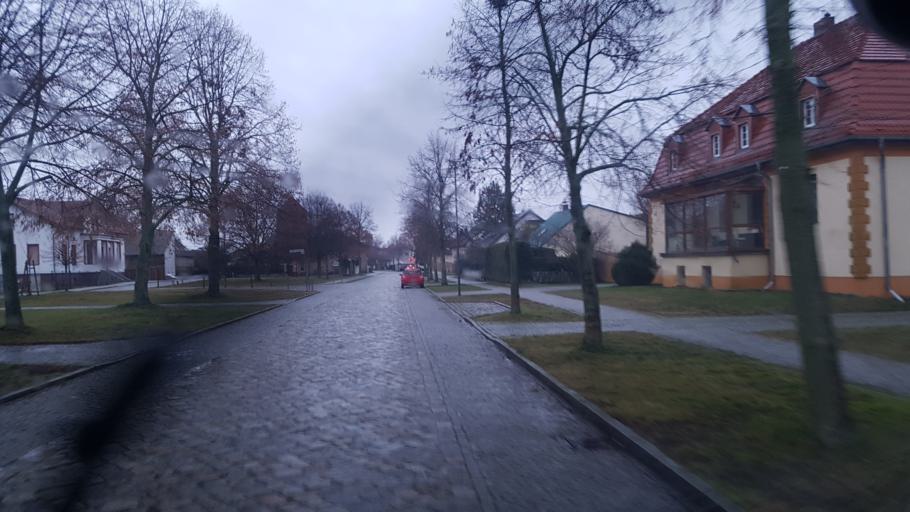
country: DE
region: Brandenburg
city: Ludwigsfelde
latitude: 52.3151
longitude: 13.1973
